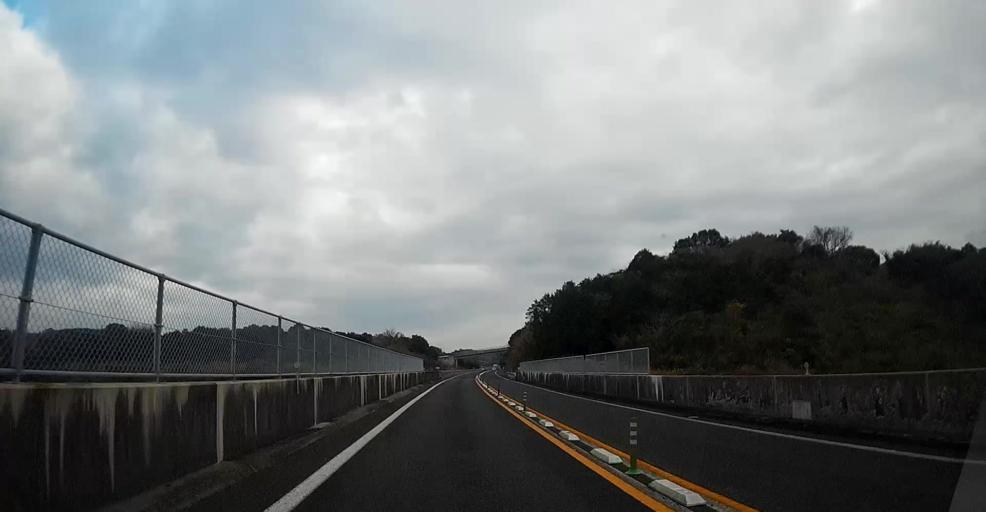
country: JP
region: Kumamoto
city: Hondo
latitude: 32.5098
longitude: 130.3230
